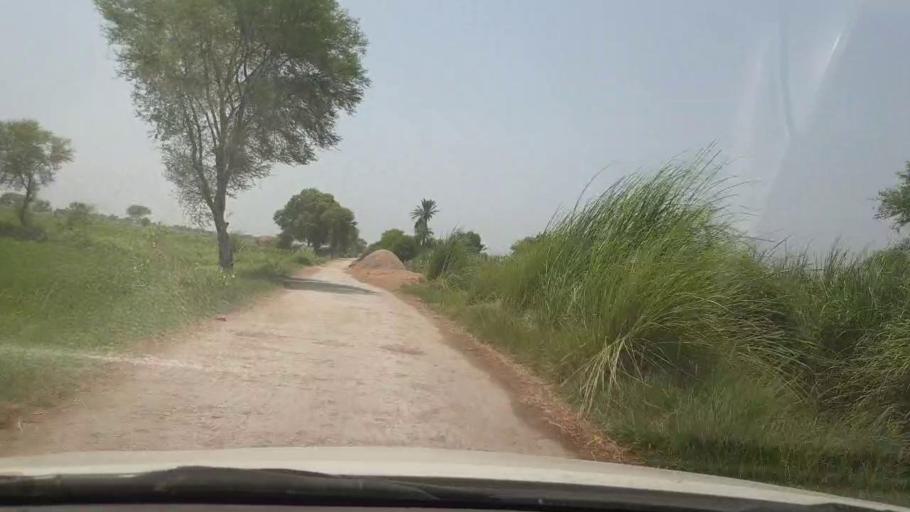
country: PK
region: Sindh
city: Shikarpur
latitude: 28.0774
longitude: 68.5486
